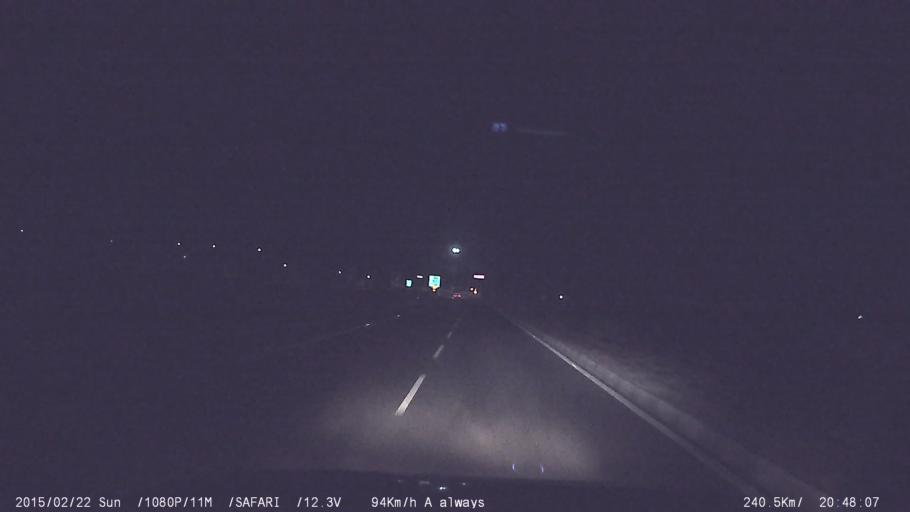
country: IN
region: Tamil Nadu
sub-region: Dindigul
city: Vedasandur
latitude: 10.5040
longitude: 77.9435
